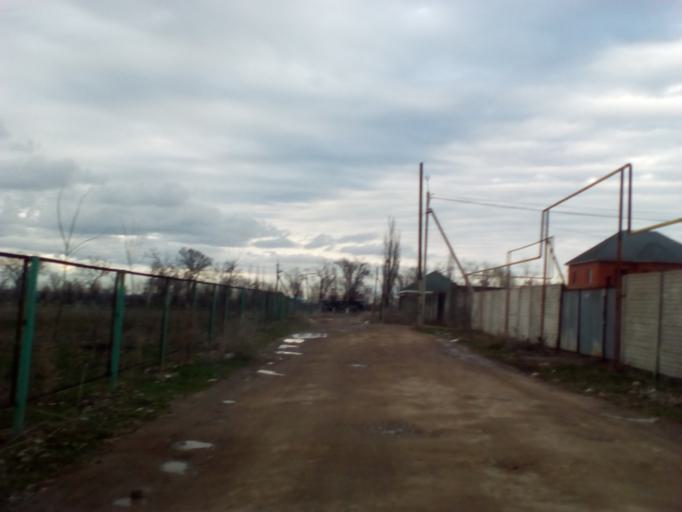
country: KZ
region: Almaty Oblysy
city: Burunday
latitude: 43.1805
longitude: 76.3996
